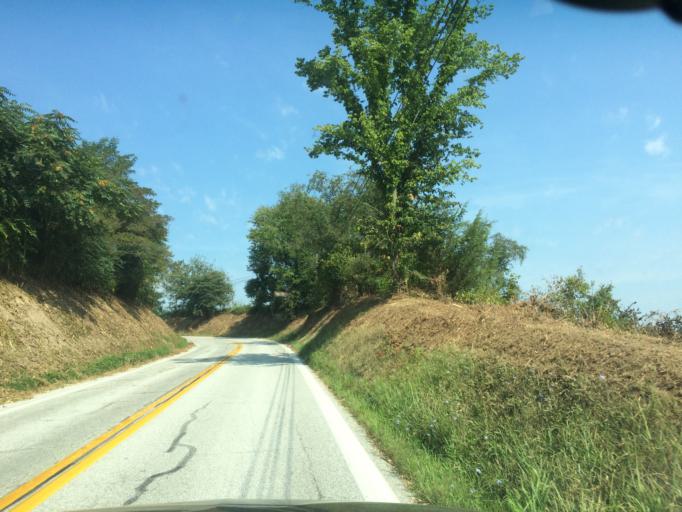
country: US
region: Maryland
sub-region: Carroll County
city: New Windsor
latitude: 39.5561
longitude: -77.1150
